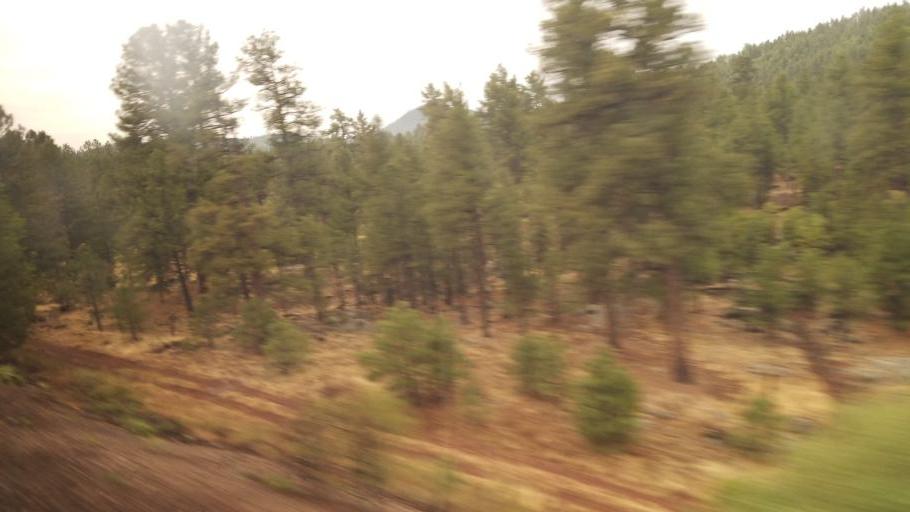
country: US
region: Arizona
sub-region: Coconino County
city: Parks
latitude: 35.2547
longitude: -111.9205
